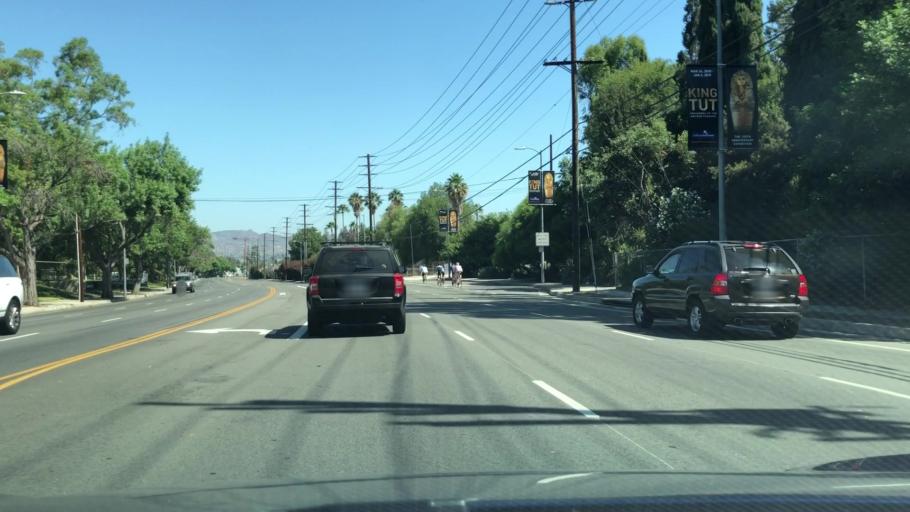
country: US
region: California
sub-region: Los Angeles County
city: Woodland Hills
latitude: 34.1739
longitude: -118.5883
